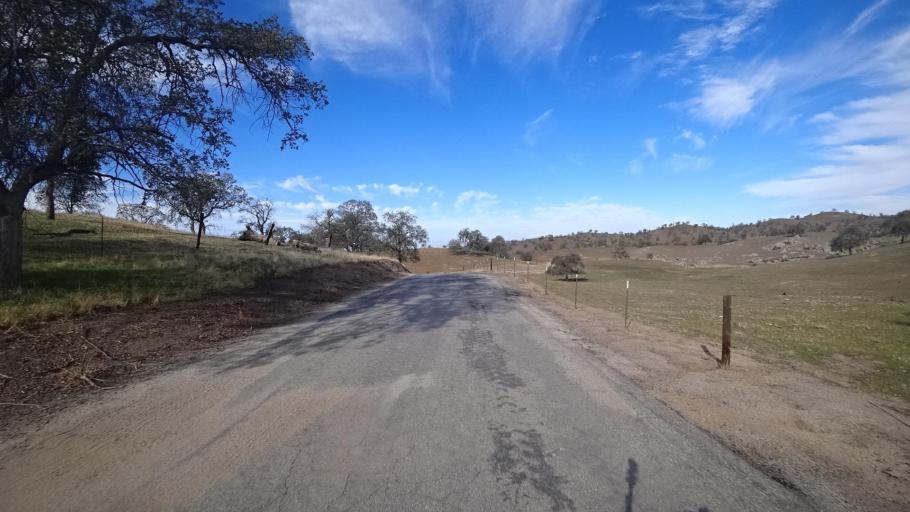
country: US
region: California
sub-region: Kern County
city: Oildale
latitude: 35.6112
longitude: -118.8385
